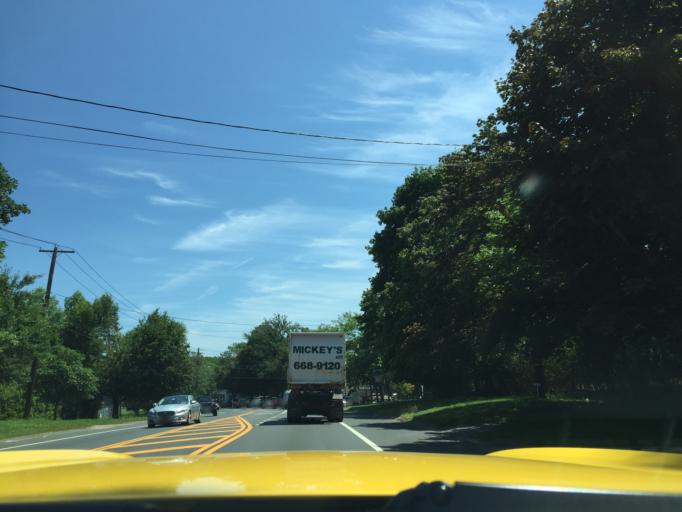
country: US
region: New York
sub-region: Suffolk County
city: Amagansett
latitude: 40.9735
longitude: -72.1449
